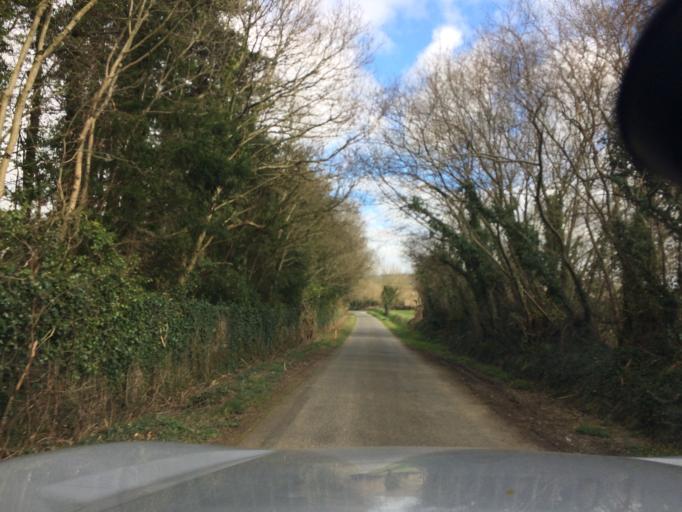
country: IE
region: Munster
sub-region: Waterford
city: Portlaw
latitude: 52.2796
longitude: -7.3789
